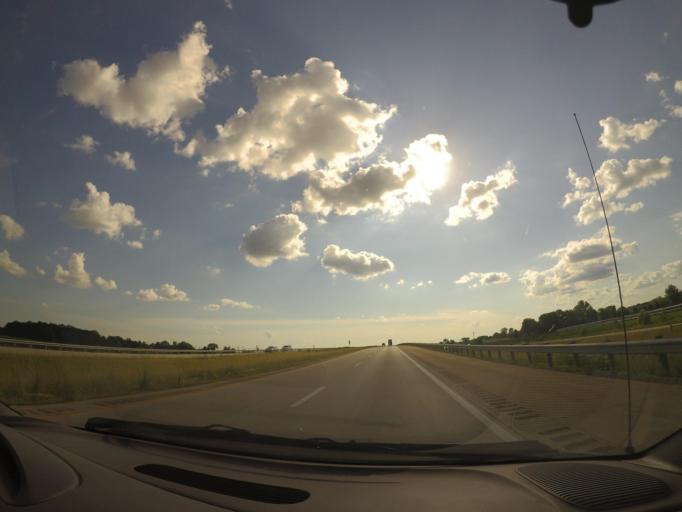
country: US
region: Ohio
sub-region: Lucas County
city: Waterville
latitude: 41.5250
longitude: -83.7295
